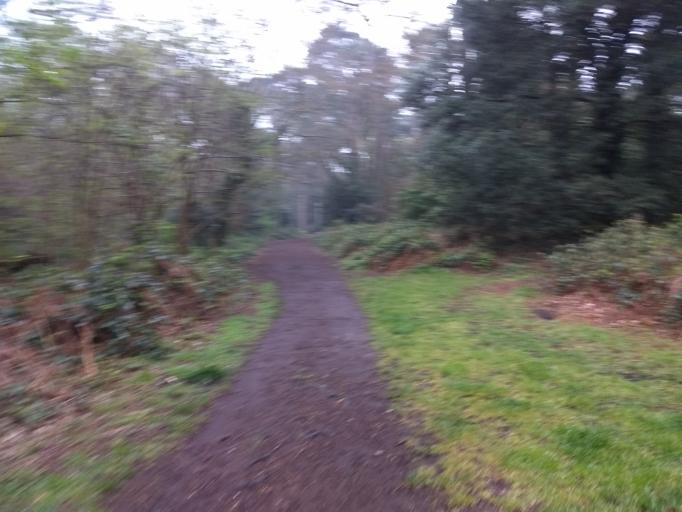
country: GB
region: England
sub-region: Dorset
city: Parkstone
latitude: 50.7213
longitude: -1.9202
